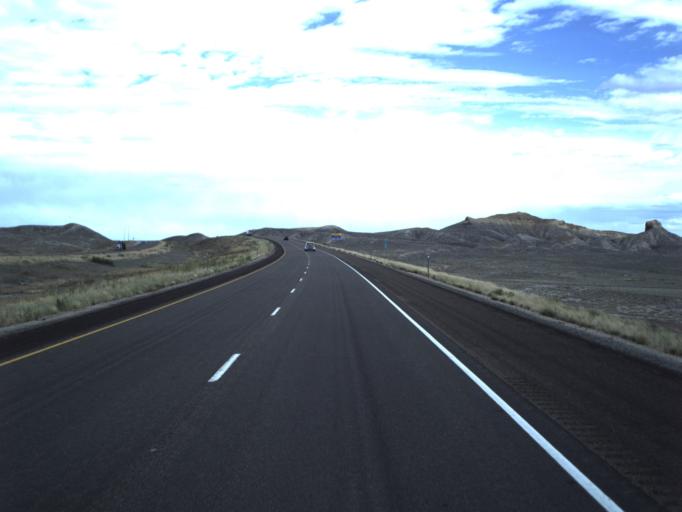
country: US
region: Utah
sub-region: Grand County
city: Moab
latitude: 38.9521
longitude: -109.6982
